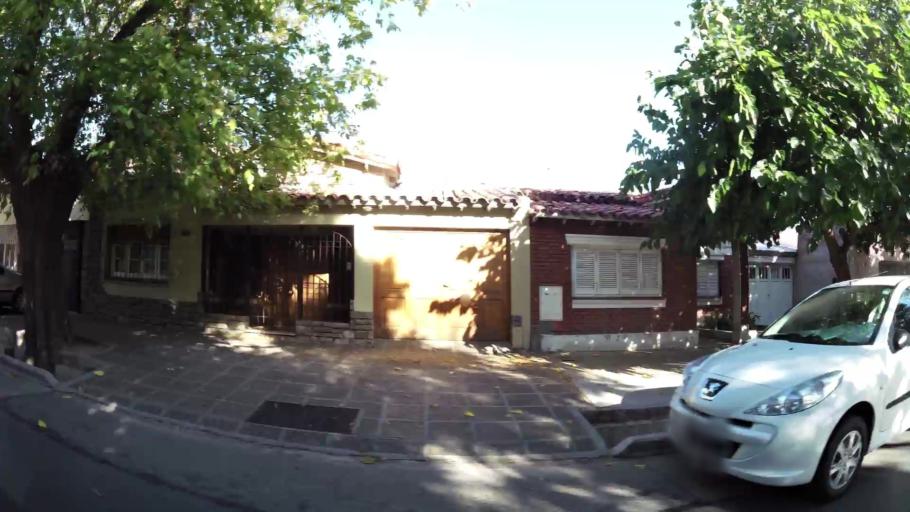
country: AR
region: Mendoza
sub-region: Departamento de Godoy Cruz
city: Godoy Cruz
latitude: -32.9355
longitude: -68.8483
